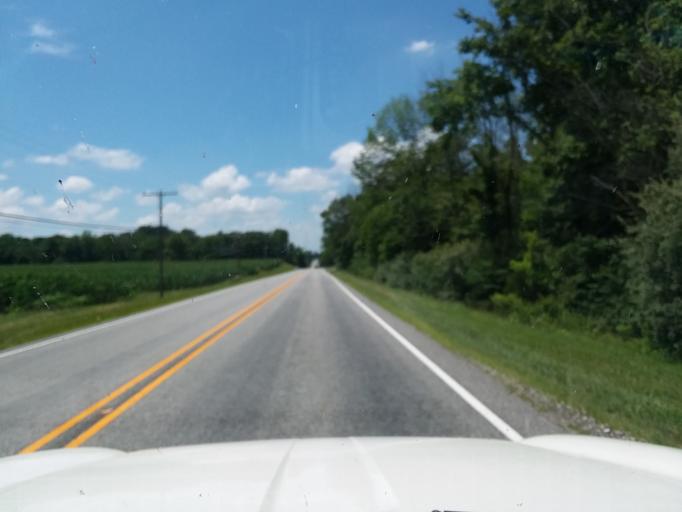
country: US
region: Indiana
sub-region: Johnson County
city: Trafalgar
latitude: 39.4091
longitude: -86.1106
